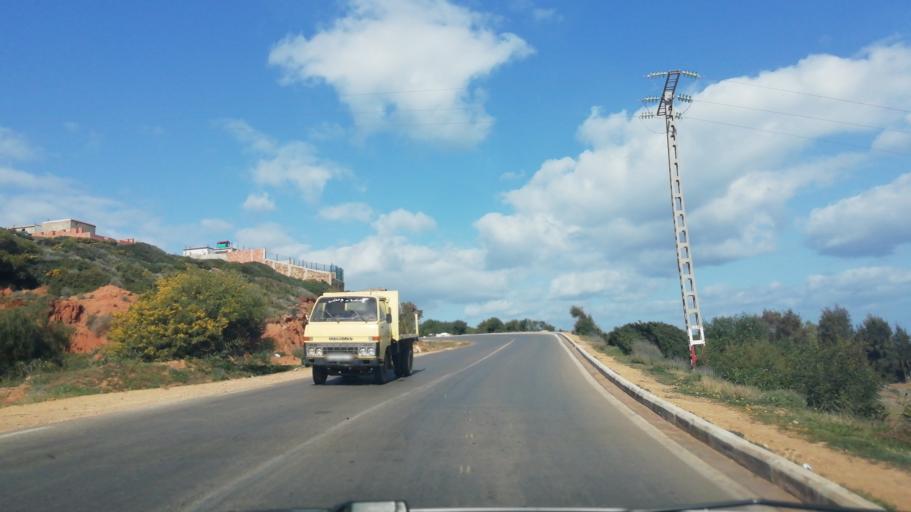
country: DZ
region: Relizane
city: Mazouna
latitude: 36.3276
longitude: 0.6912
